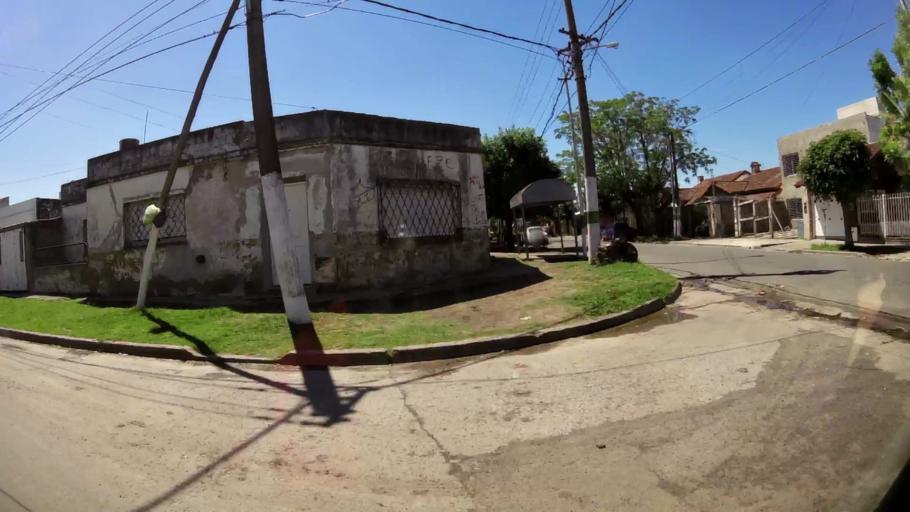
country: AR
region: Buenos Aires
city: Ituzaingo
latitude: -34.6761
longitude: -58.6598
